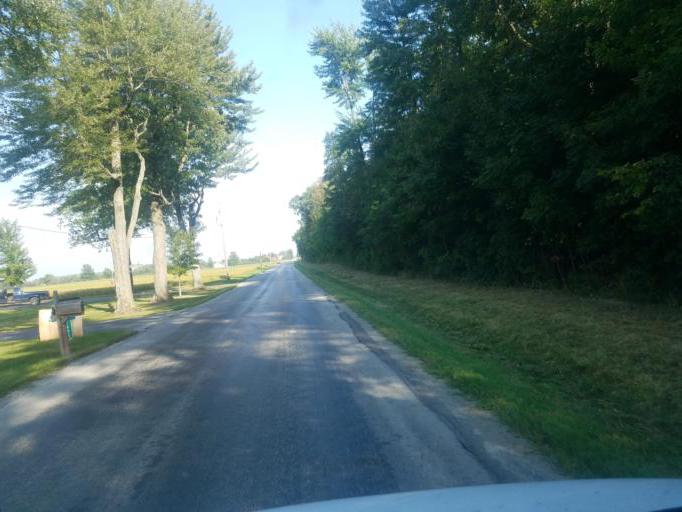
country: US
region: Ohio
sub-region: Wyandot County
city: Carey
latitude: 40.9051
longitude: -83.4319
